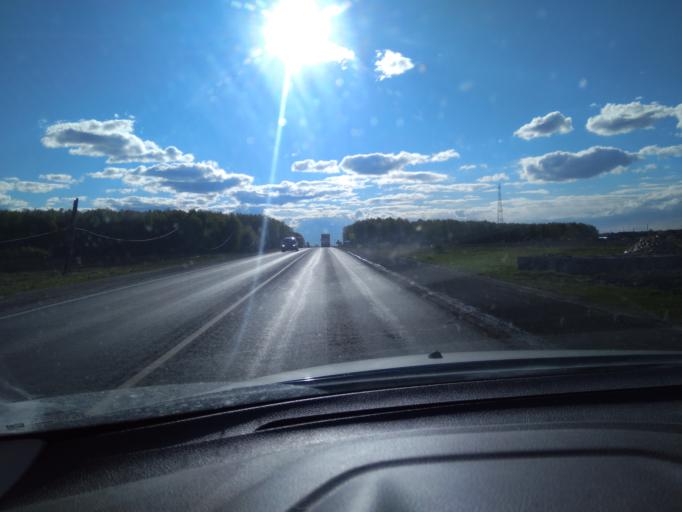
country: RU
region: Sverdlovsk
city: Zavodouspenskoye
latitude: 57.0711
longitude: 64.9474
